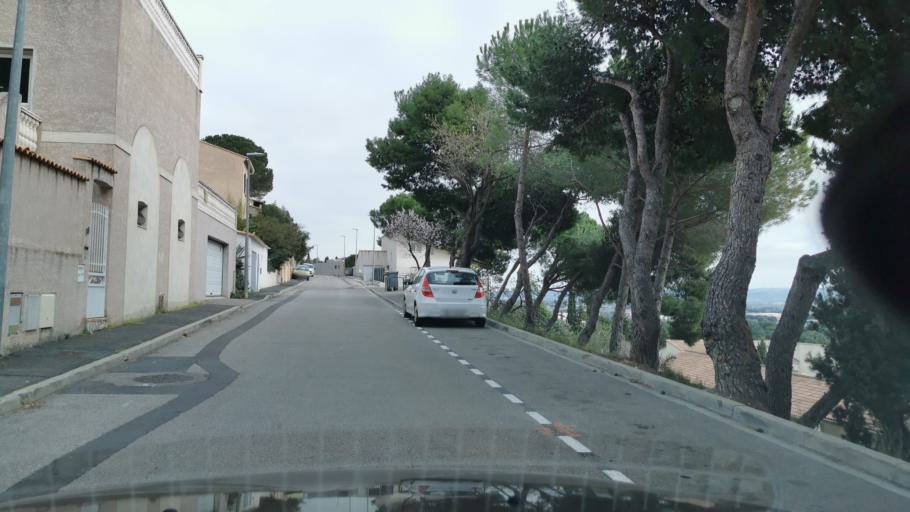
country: FR
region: Languedoc-Roussillon
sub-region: Departement de l'Aude
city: Narbonne
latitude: 43.1642
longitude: 2.9773
